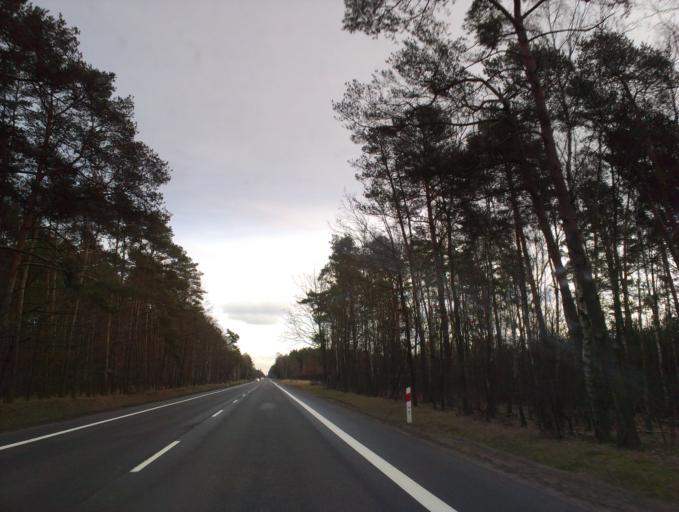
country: PL
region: Masovian Voivodeship
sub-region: Powiat sierpecki
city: Szczutowo
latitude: 52.8788
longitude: 19.6002
